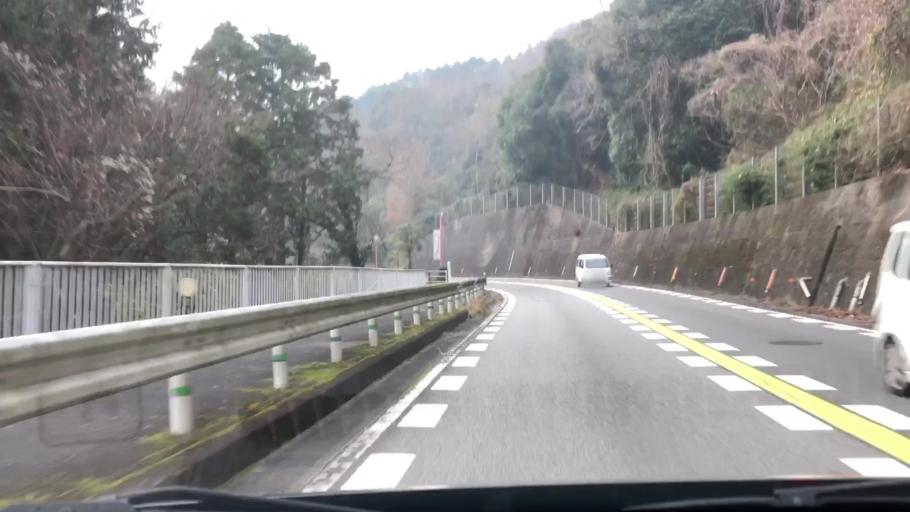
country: JP
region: Oita
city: Usuki
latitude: 33.0252
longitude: 131.6943
